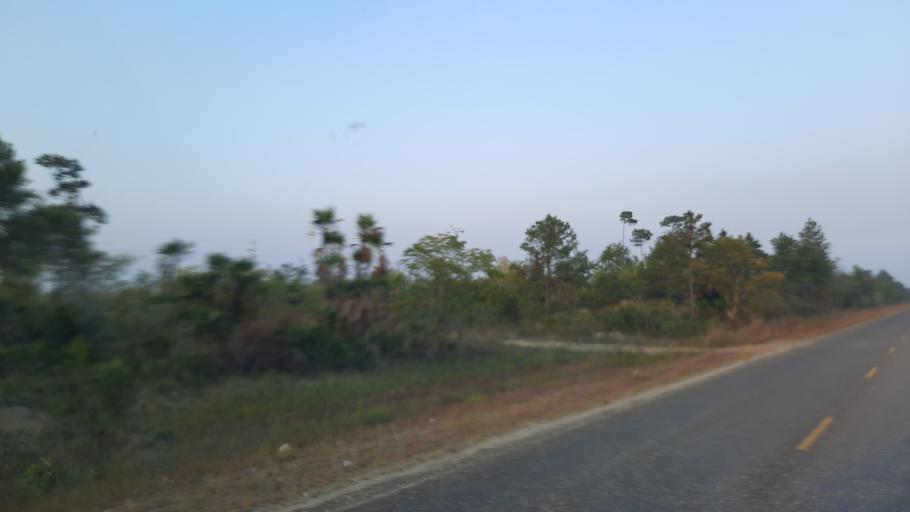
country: BZ
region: Stann Creek
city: Placencia
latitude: 16.5340
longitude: -88.4876
